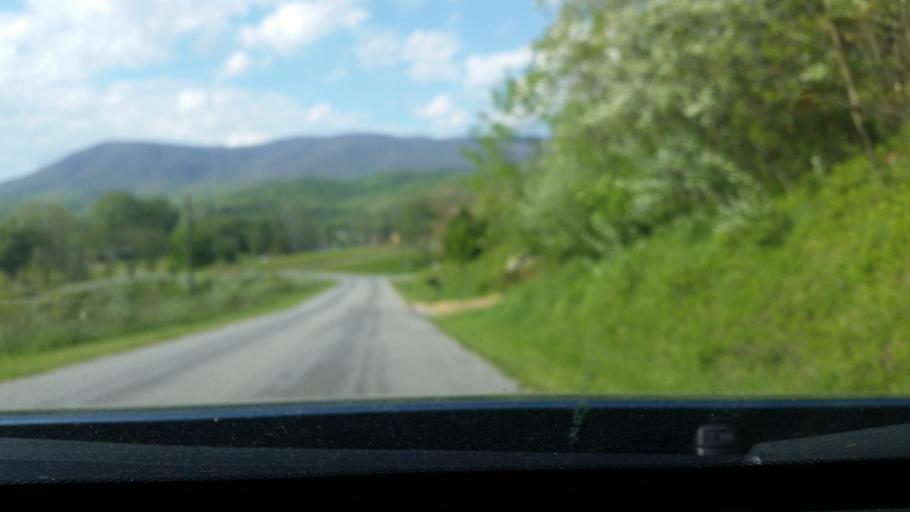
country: US
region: Virginia
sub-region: Giles County
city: Pembroke
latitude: 37.3096
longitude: -80.6325
